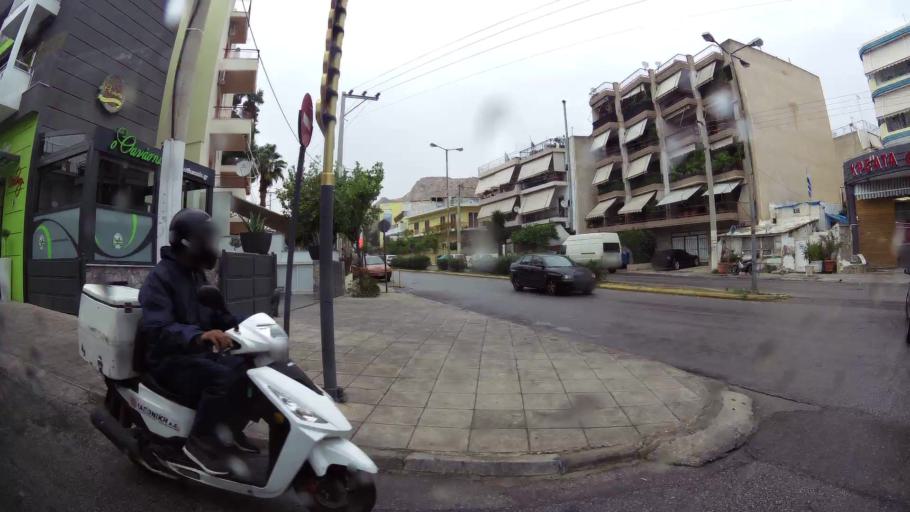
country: GR
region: Attica
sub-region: Nomos Piraios
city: Korydallos
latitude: 37.9863
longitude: 23.6420
